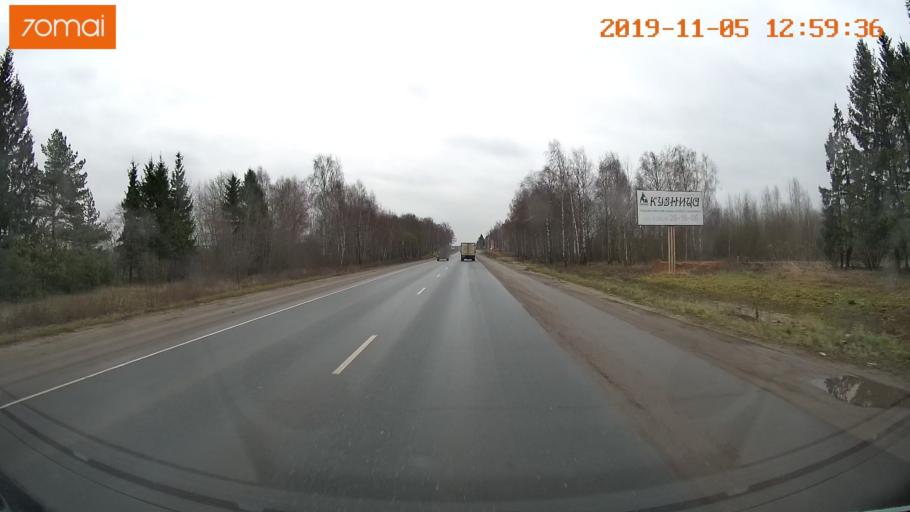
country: RU
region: Ivanovo
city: Kokhma
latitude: 56.9176
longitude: 41.1321
